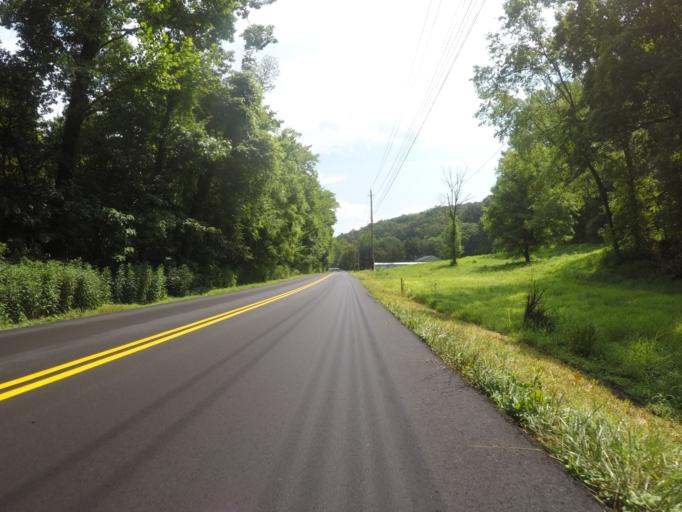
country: US
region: Kentucky
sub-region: Boyd County
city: Ironville
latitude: 38.4536
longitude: -82.6840
